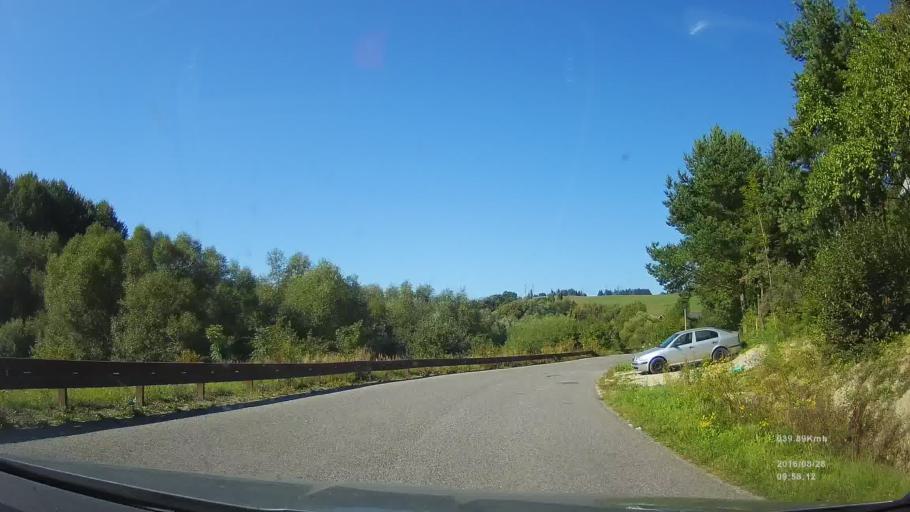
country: SK
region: Zilinsky
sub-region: Okres Liptovsky Mikulas
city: Liptovsky Mikulas
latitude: 49.1167
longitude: 19.4800
